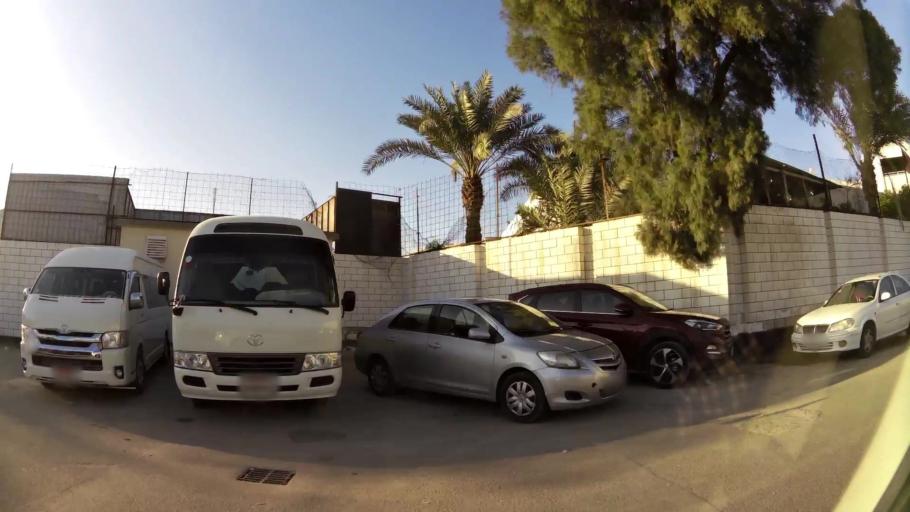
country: BH
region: Manama
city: Manama
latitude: 26.2338
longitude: 50.5901
